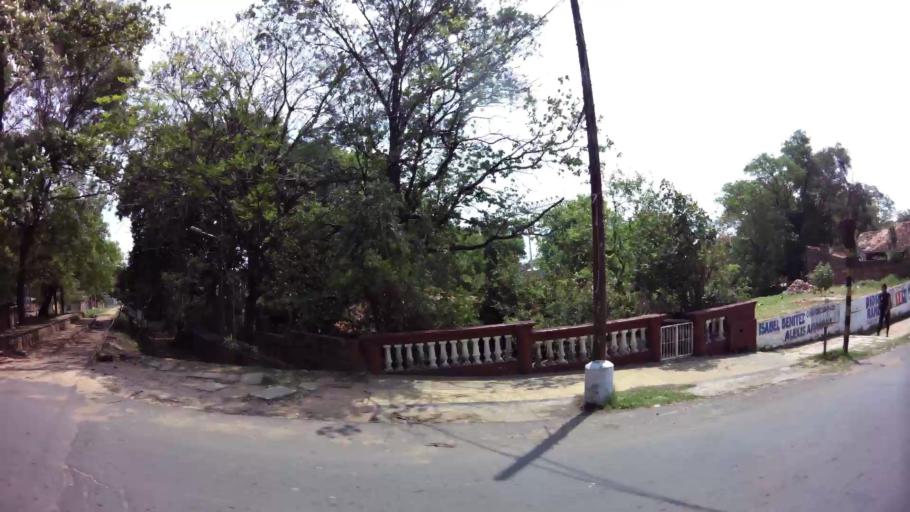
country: PY
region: Asuncion
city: Asuncion
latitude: -25.2774
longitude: -57.6098
